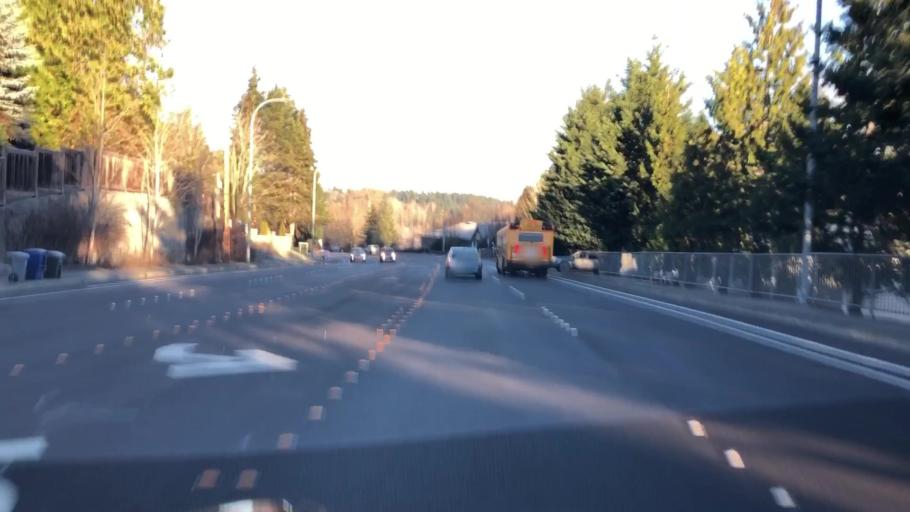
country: US
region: Washington
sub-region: King County
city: Newport
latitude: 47.5928
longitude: -122.1644
